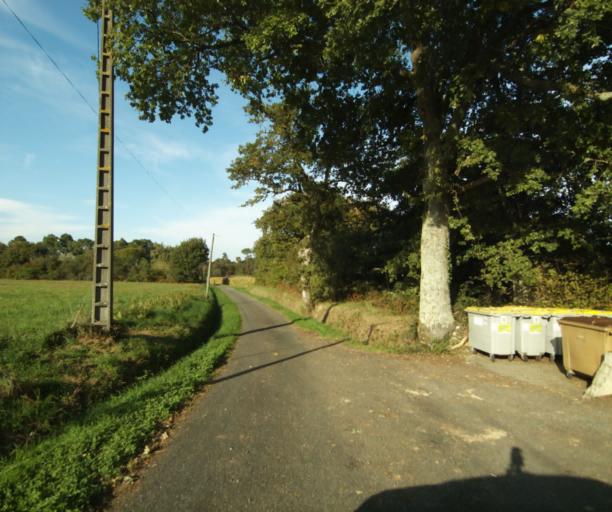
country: FR
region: Midi-Pyrenees
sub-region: Departement du Gers
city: Eauze
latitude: 43.8695
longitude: 0.0507
